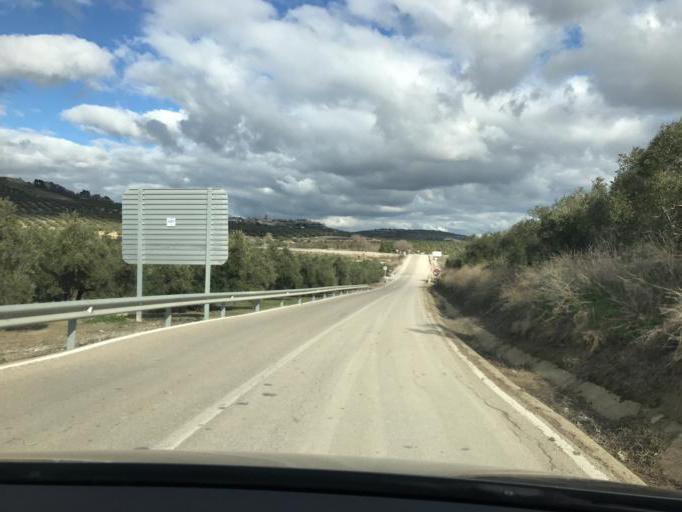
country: ES
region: Andalusia
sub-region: Provincia de Jaen
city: Ubeda
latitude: 37.9919
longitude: -3.3871
